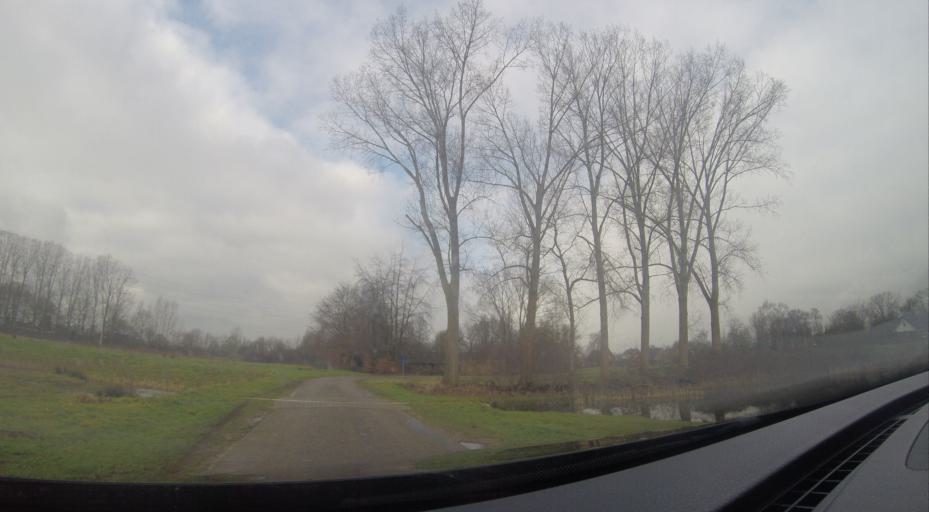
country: NL
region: Gelderland
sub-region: Gemeente Doetinchem
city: Doetinchem
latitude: 51.9554
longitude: 6.2775
